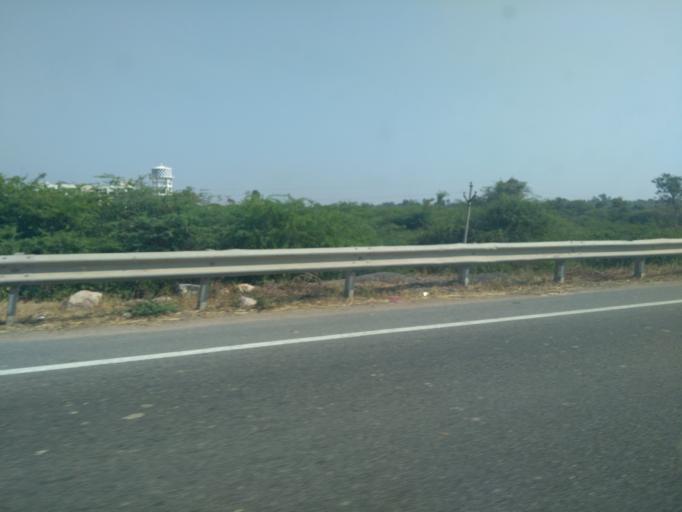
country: IN
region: Telangana
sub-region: Mahbubnagar
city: Wanparti
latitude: 16.4472
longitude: 77.9377
